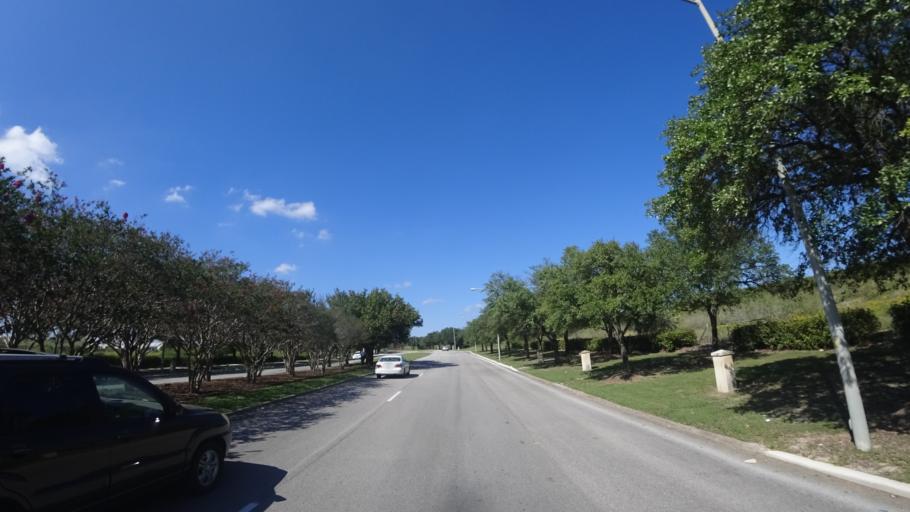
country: US
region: Texas
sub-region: Travis County
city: Manor
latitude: 30.3358
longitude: -97.6078
